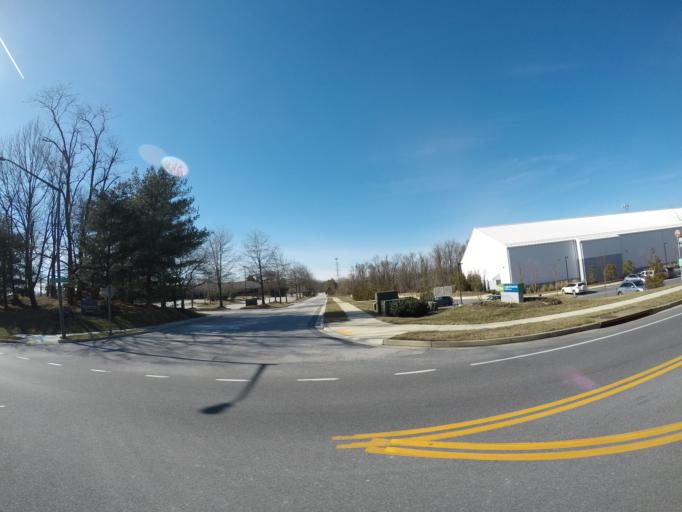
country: US
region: Maryland
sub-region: Howard County
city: Columbia
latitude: 39.2028
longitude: -76.8131
